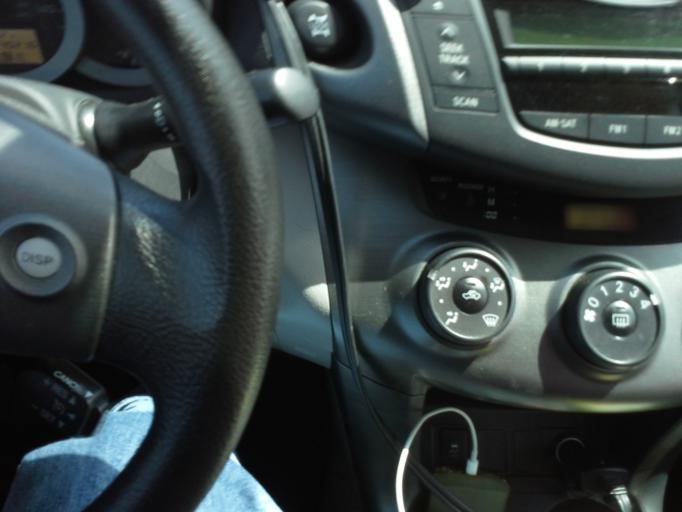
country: TM
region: Ahal
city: Ashgabat
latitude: 38.0011
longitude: 58.4058
